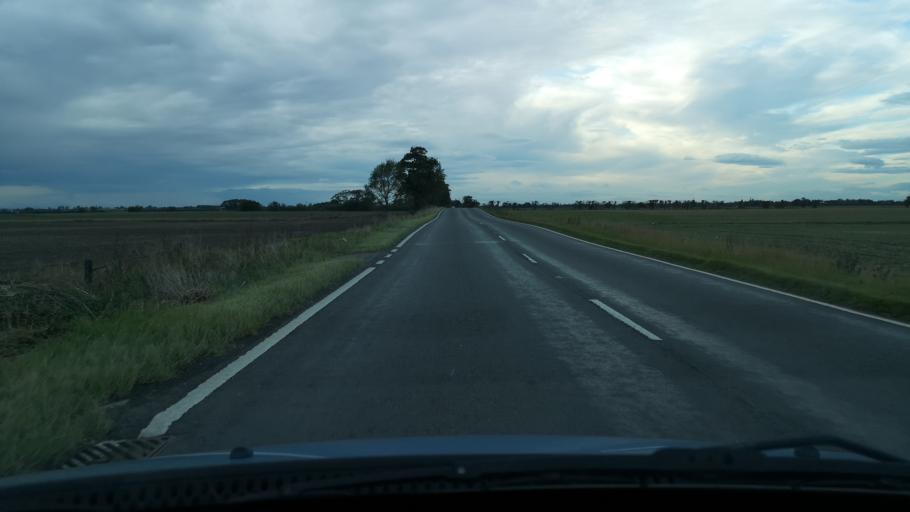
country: GB
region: England
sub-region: Doncaster
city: Hatfield
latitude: 53.5892
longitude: -0.9252
